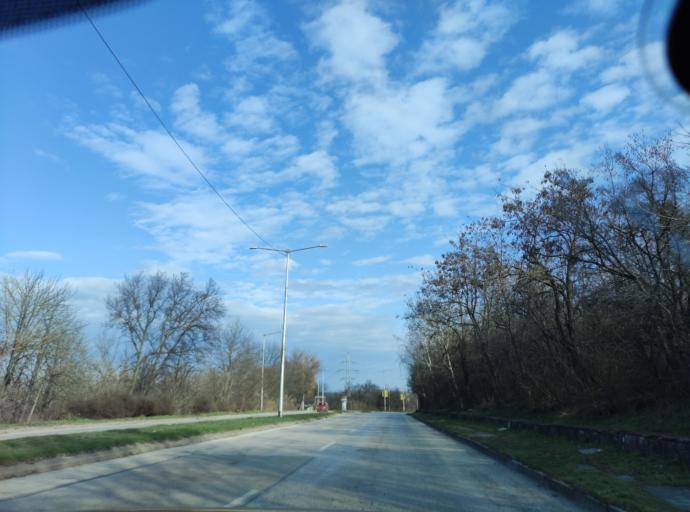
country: BG
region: Pleven
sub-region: Obshtina Pleven
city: Pleven
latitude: 43.4345
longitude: 24.5711
